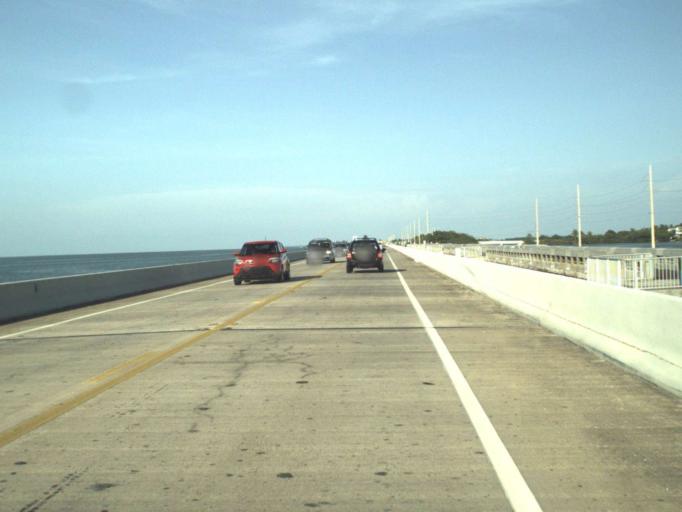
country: US
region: Florida
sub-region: Monroe County
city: Marathon
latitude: 24.7774
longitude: -80.9227
